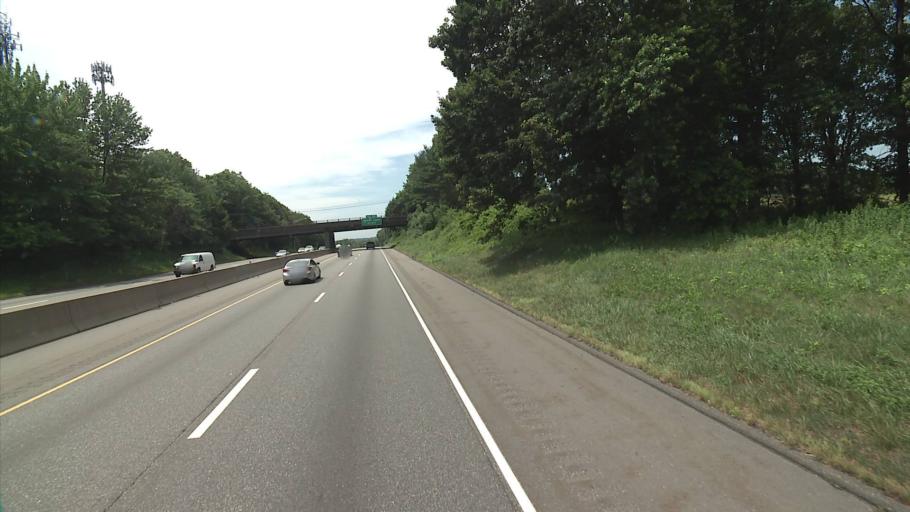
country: US
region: Connecticut
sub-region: New Haven County
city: Guilford Center
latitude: 41.2893
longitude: -72.6568
